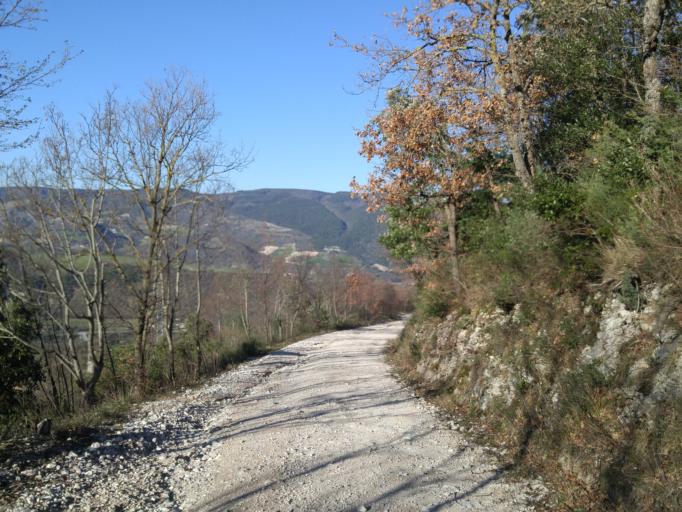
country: IT
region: The Marches
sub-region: Provincia di Pesaro e Urbino
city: Canavaccio
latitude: 43.6534
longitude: 12.7463
